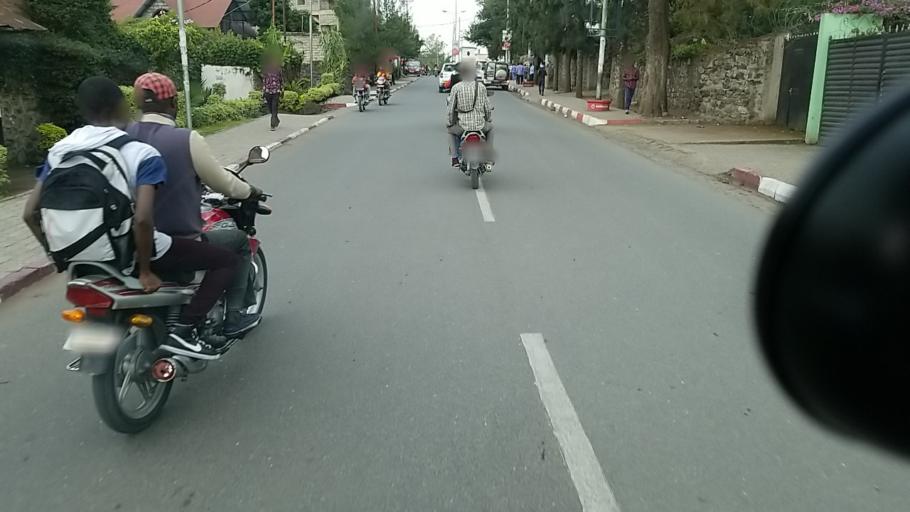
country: RW
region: Western Province
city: Gisenyi
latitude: -1.6980
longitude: 29.2420
